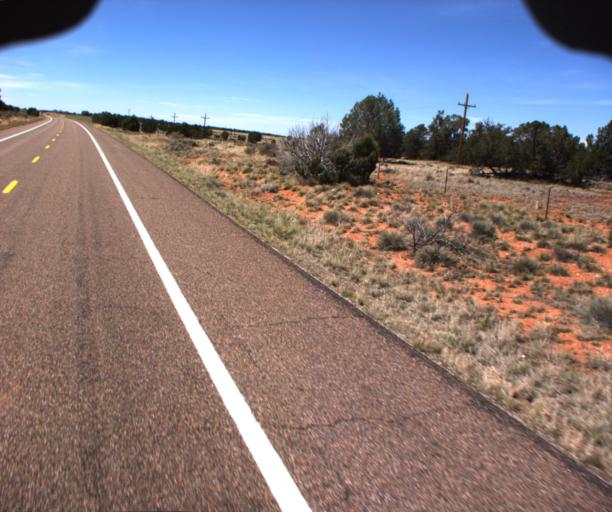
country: US
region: Arizona
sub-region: Mohave County
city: Peach Springs
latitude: 35.5120
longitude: -113.1906
